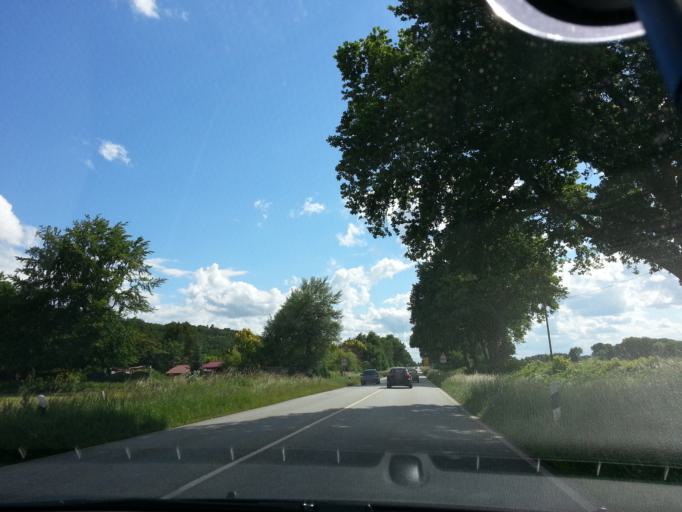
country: DE
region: Schleswig-Holstein
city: Fredeburg
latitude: 53.6503
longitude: 10.7074
